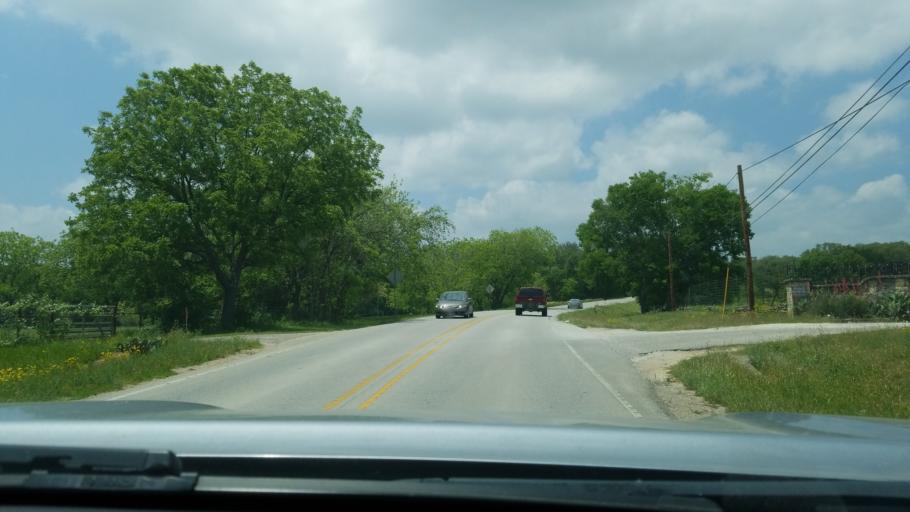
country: US
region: Texas
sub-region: Hays County
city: Dripping Springs
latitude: 30.1315
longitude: -98.0169
